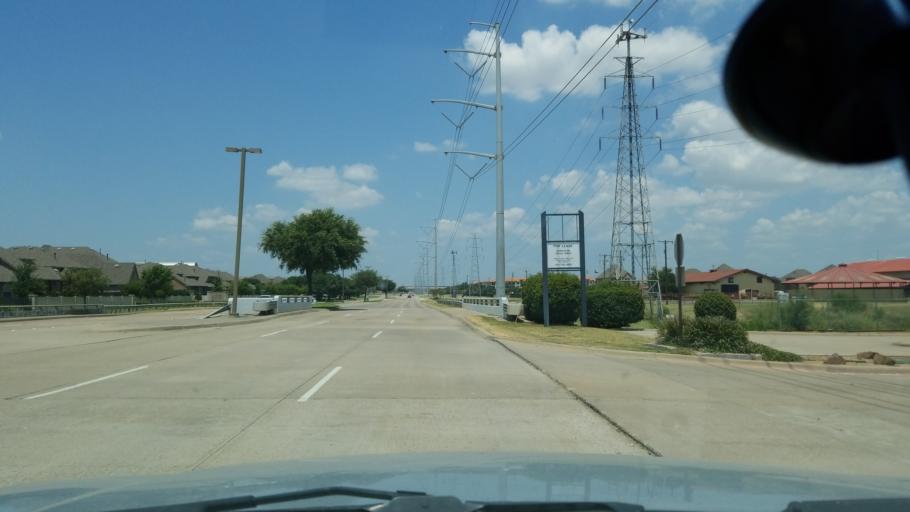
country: US
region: Texas
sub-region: Dallas County
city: Farmers Branch
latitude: 32.8904
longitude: -96.9358
